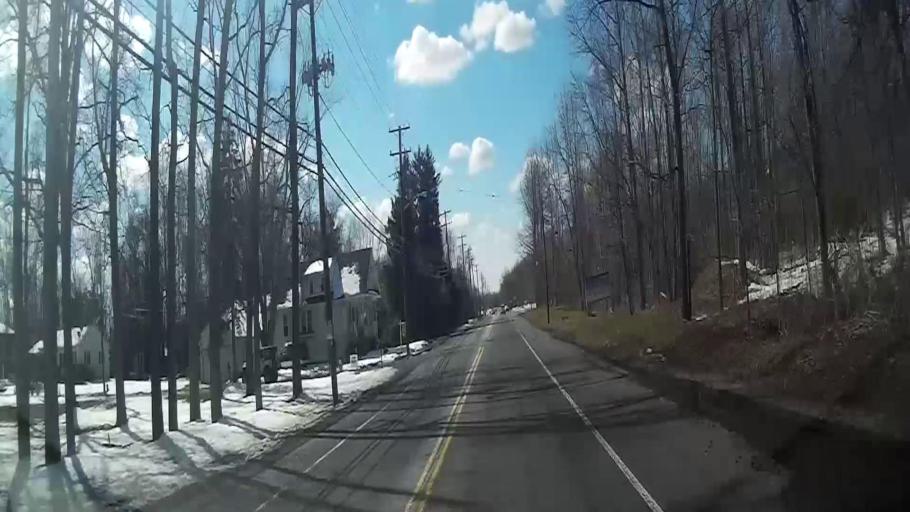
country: US
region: New Jersey
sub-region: Burlington County
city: Marlton
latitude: 39.8844
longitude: -74.8822
